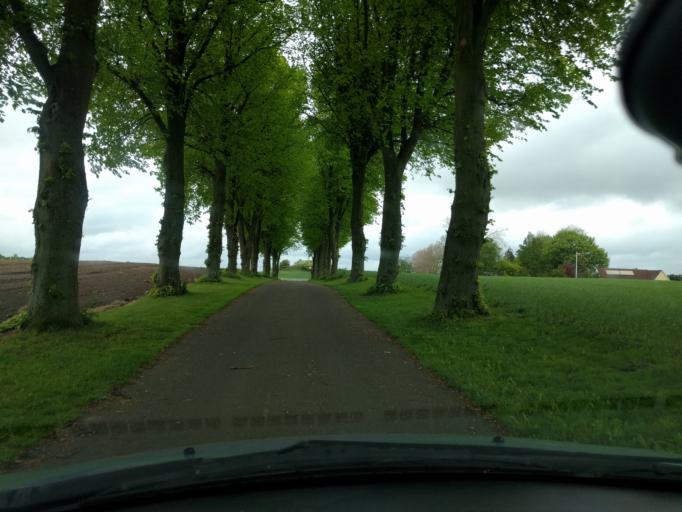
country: DK
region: South Denmark
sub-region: Nyborg Kommune
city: Ullerslev
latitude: 55.3550
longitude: 10.7147
